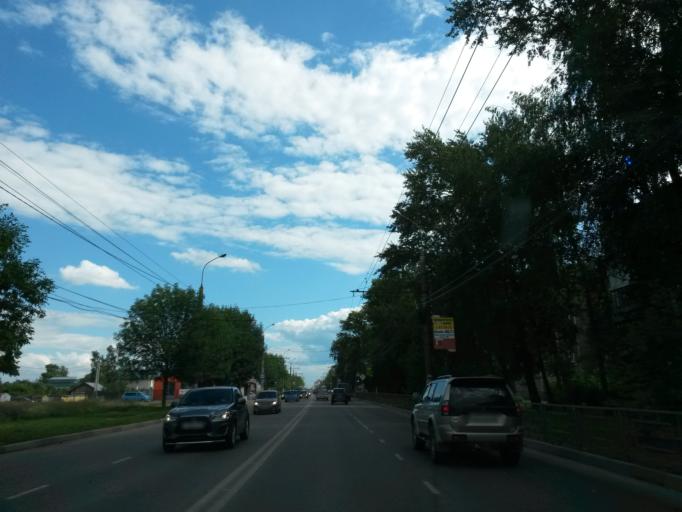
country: RU
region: Ivanovo
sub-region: Gorod Ivanovo
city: Ivanovo
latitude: 56.9742
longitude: 41.0088
